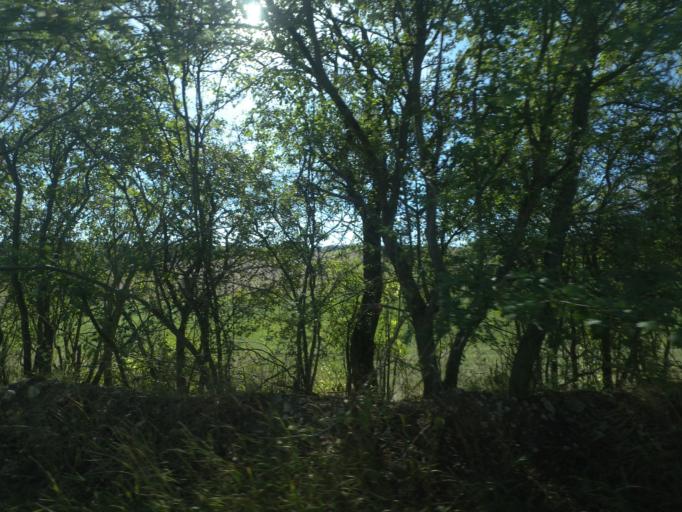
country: DE
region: Thuringia
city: Rottenbach
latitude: 50.7500
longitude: 11.1907
